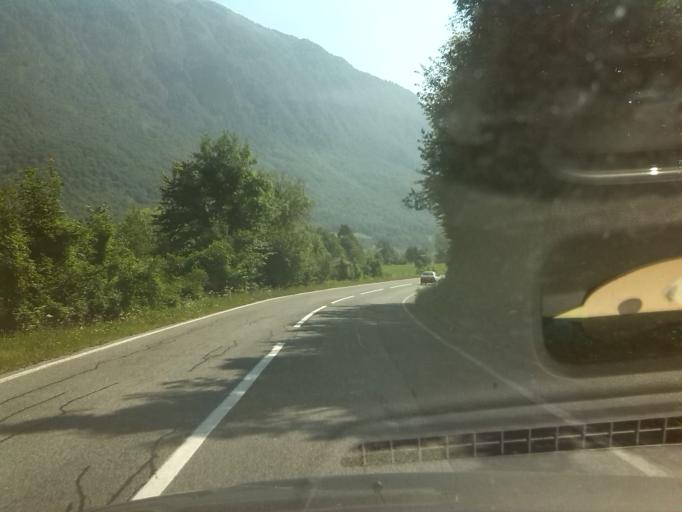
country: IT
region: Friuli Venezia Giulia
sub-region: Provincia di Udine
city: Cras
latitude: 46.2046
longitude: 13.6633
